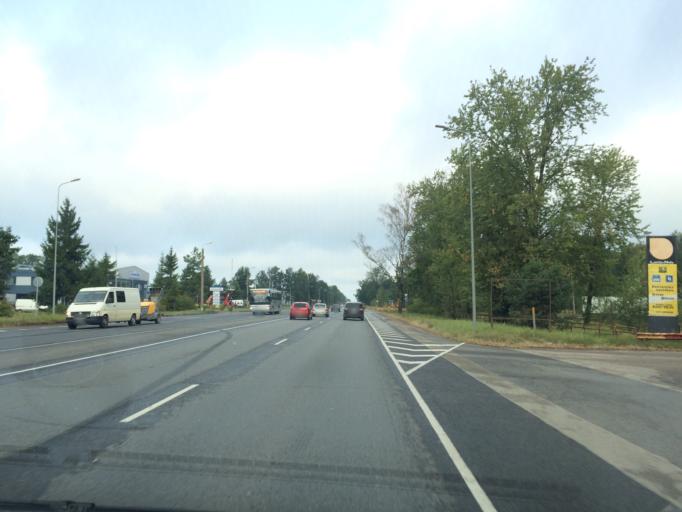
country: LV
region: Kekava
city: Kekava
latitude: 56.8772
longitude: 24.2579
